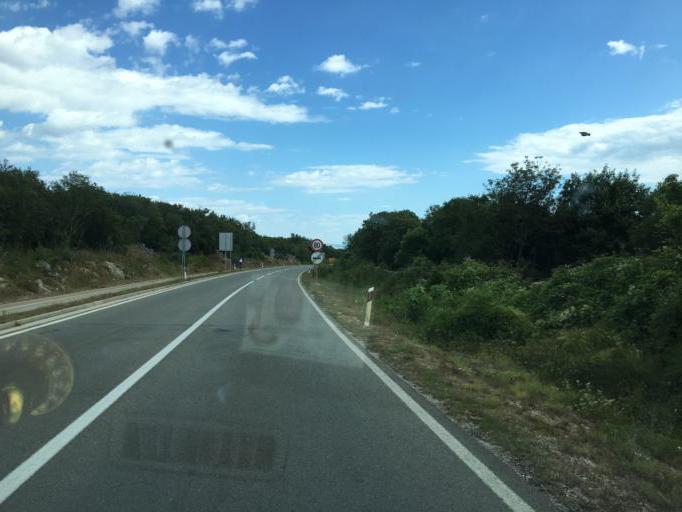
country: HR
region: Primorsko-Goranska
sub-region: Grad Krk
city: Krk
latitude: 45.0415
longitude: 14.5710
